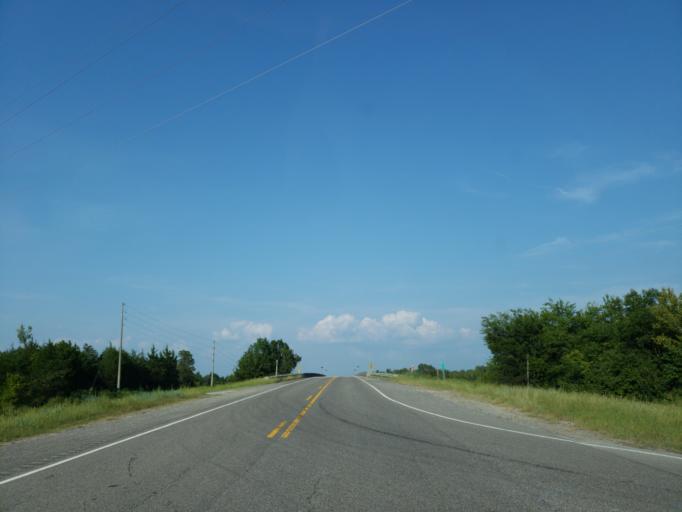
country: US
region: Alabama
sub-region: Sumter County
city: Livingston
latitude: 32.6935
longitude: -88.1164
